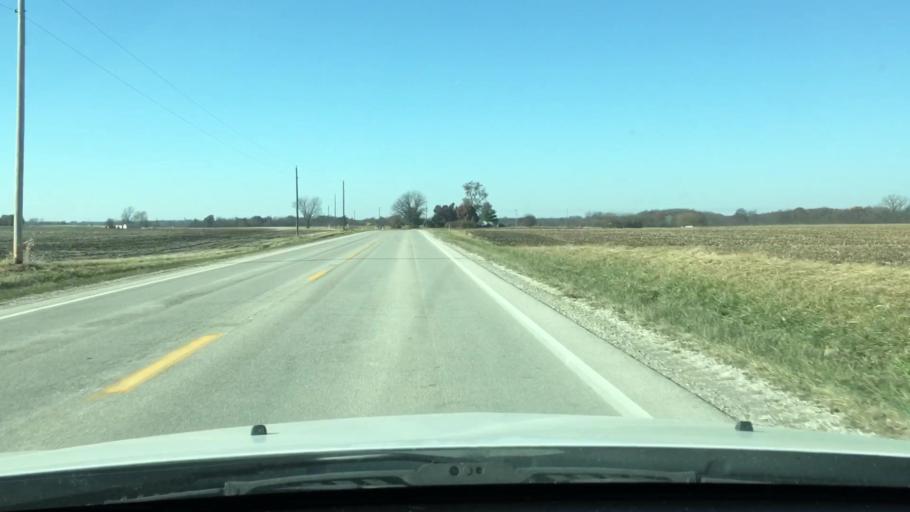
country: US
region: Illinois
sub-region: Pike County
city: Pittsfield
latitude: 39.6195
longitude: -90.7183
